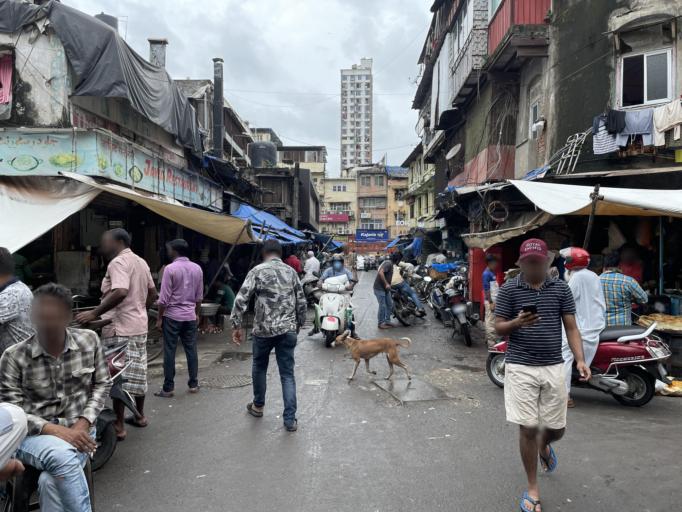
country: IN
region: Maharashtra
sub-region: Mumbai Suburban
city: Mumbai
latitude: 18.9591
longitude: 72.8291
